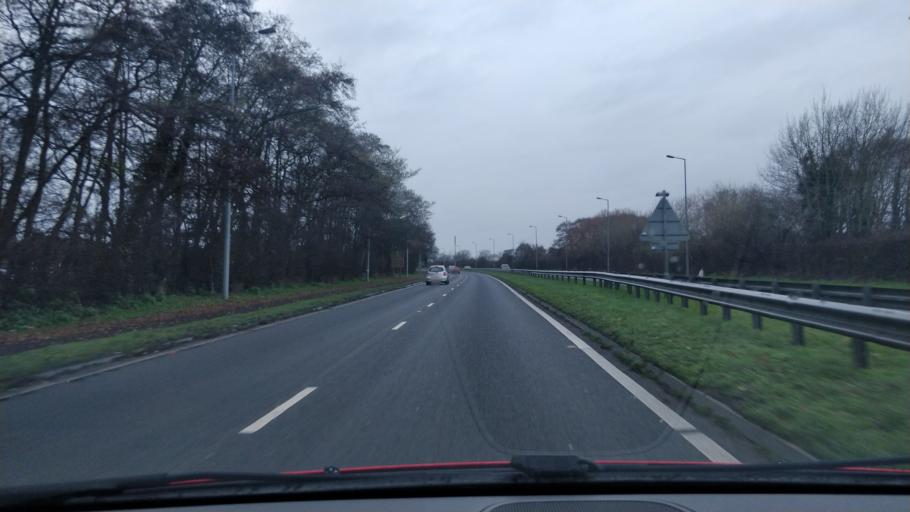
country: GB
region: England
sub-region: Sefton
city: Formby
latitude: 53.5643
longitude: -3.0465
